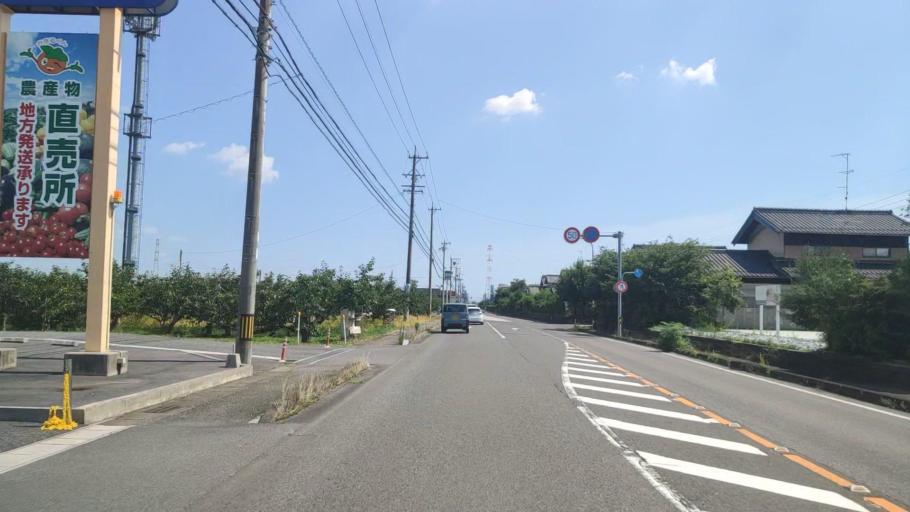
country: JP
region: Gifu
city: Godo
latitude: 35.4690
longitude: 136.6752
